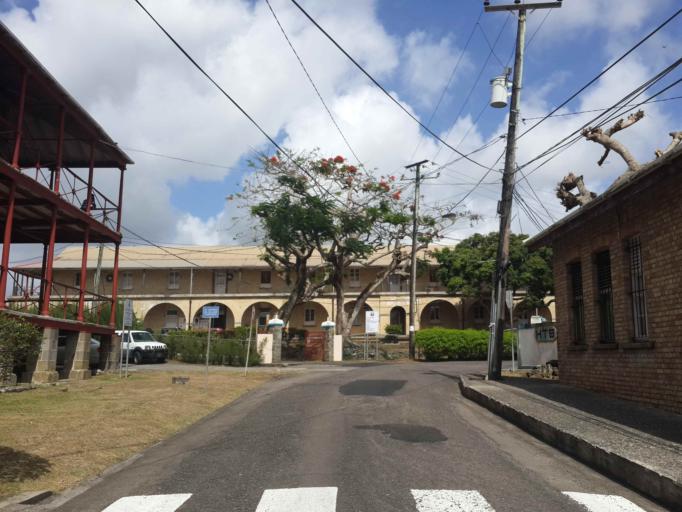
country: LC
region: Castries Quarter
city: Castries
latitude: 13.9991
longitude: -60.9957
